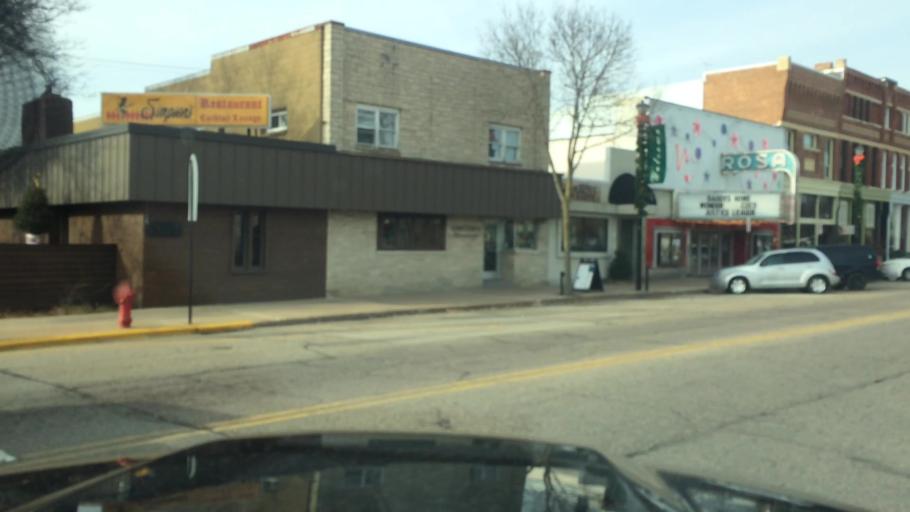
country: US
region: Wisconsin
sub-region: Waupaca County
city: Waupaca
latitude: 44.3561
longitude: -89.0848
